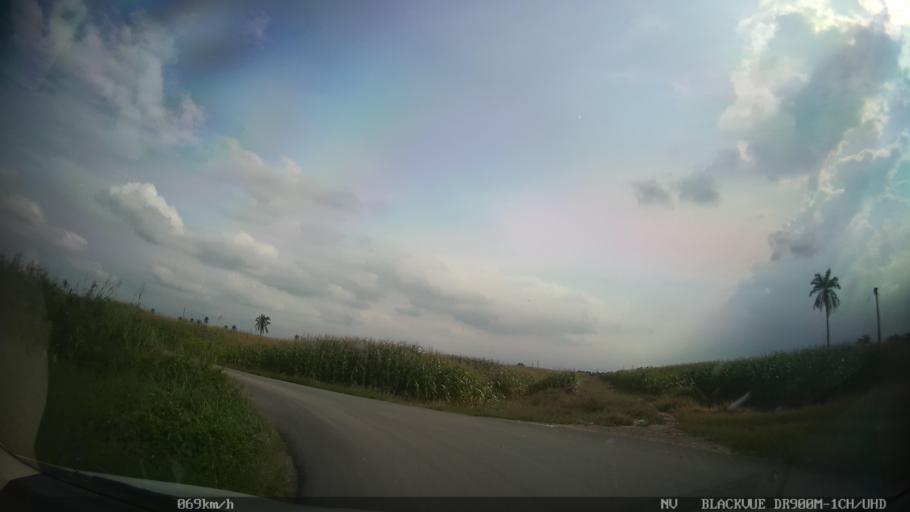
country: ID
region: North Sumatra
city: Percut
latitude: 3.5707
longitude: 98.7767
